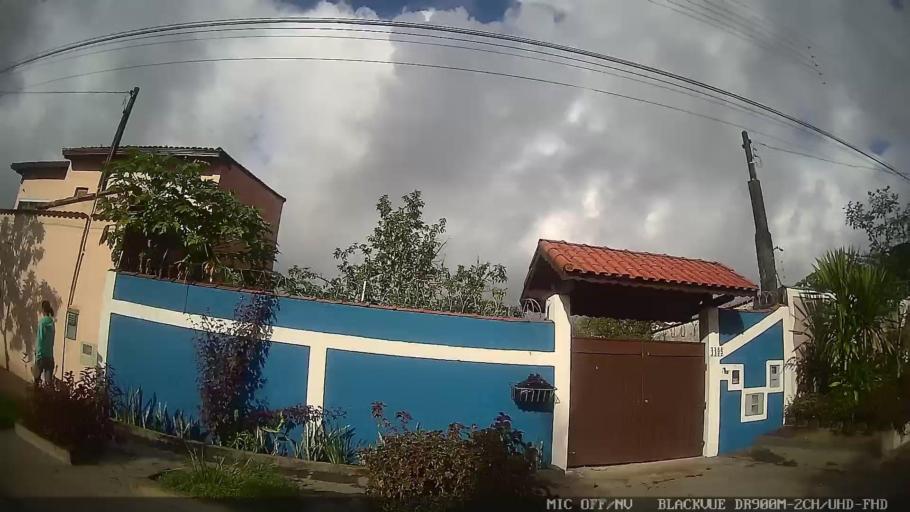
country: BR
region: Sao Paulo
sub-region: Itanhaem
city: Itanhaem
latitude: -24.1923
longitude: -46.8640
